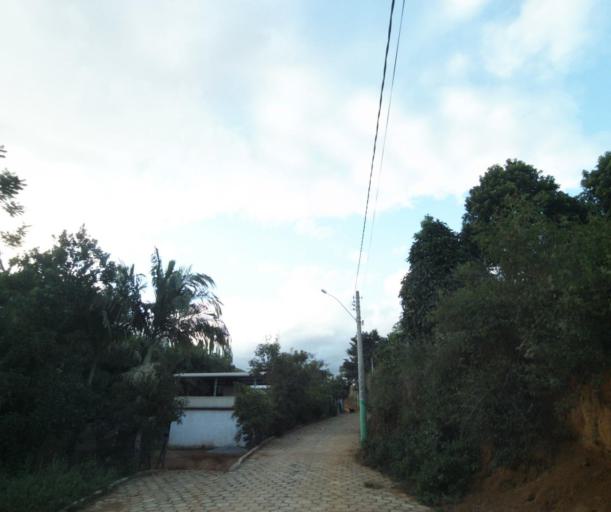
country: BR
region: Espirito Santo
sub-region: Guacui
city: Guacui
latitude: -20.6172
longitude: -41.6843
